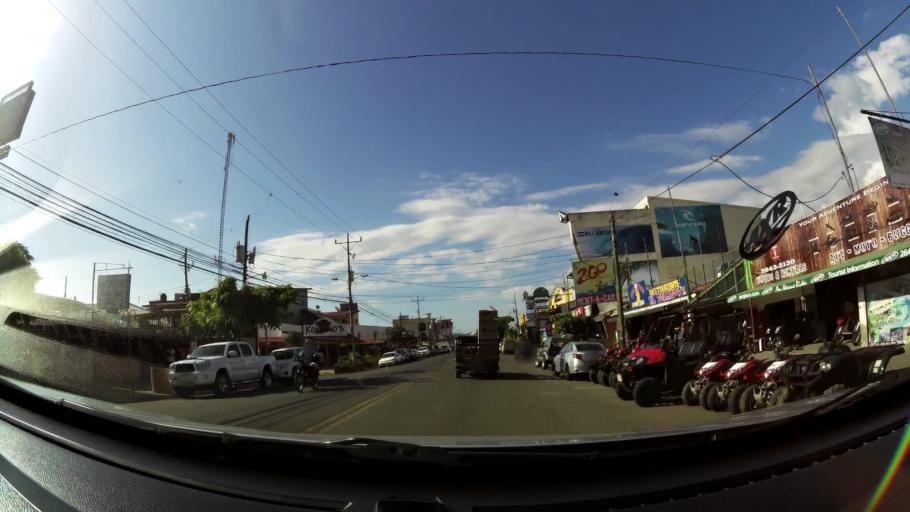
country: CR
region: Puntarenas
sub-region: Canton de Garabito
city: Jaco
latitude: 9.6122
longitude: -84.6261
